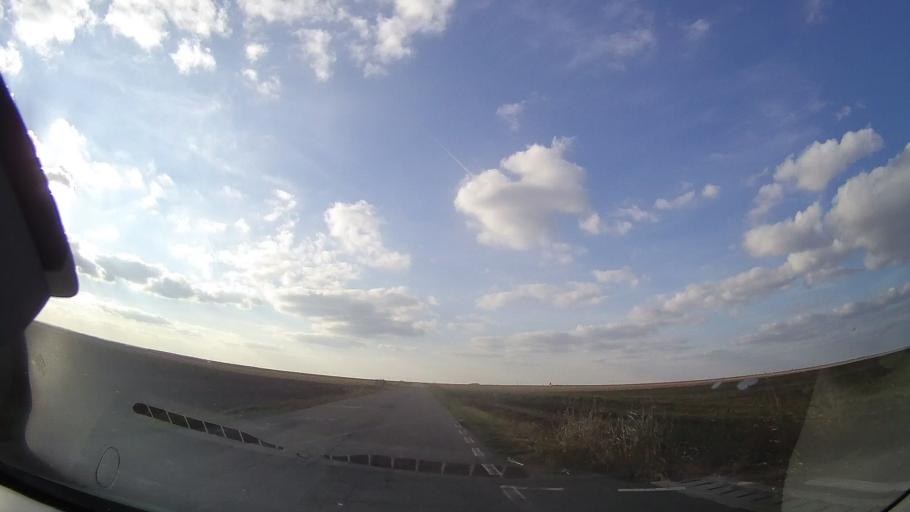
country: RO
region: Constanta
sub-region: Comuna Cerchezu
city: Cerchezu
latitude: 43.8246
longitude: 28.1381
